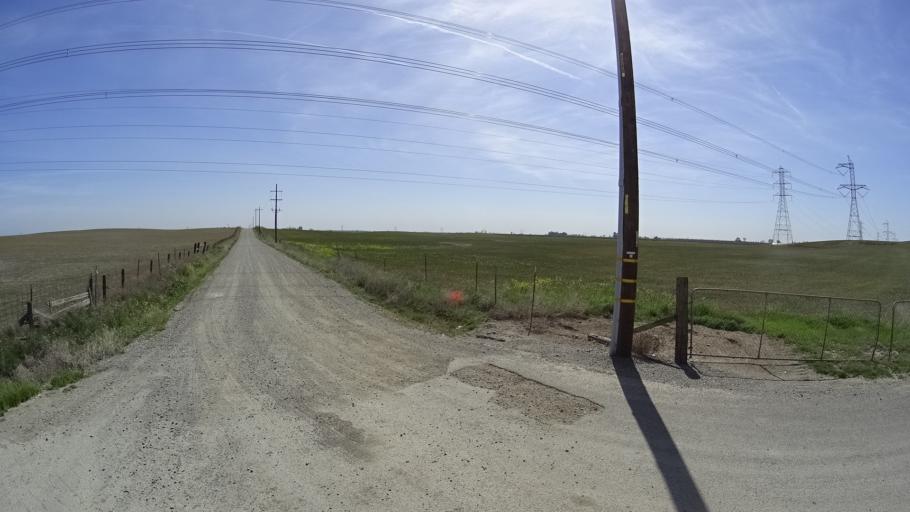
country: US
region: California
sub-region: Glenn County
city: Willows
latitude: 39.5390
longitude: -122.2870
